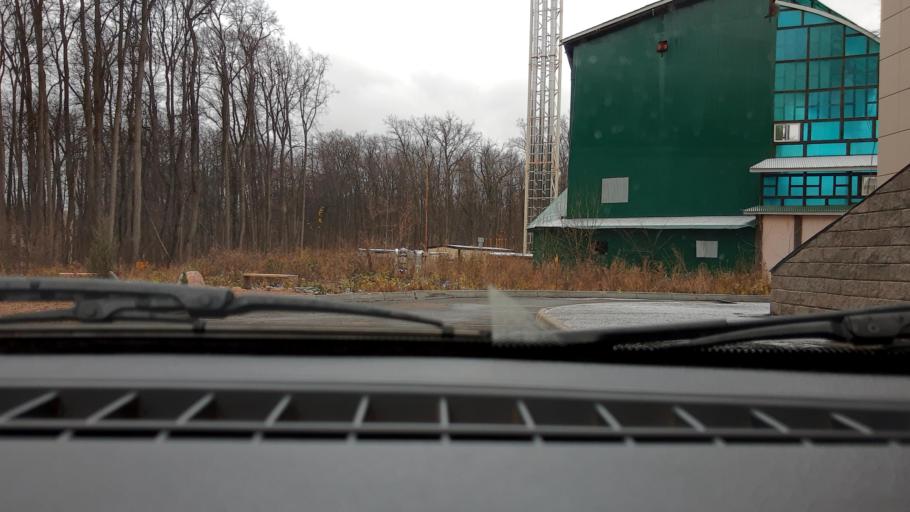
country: RU
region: Bashkortostan
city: Ufa
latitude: 54.7680
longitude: 56.0068
